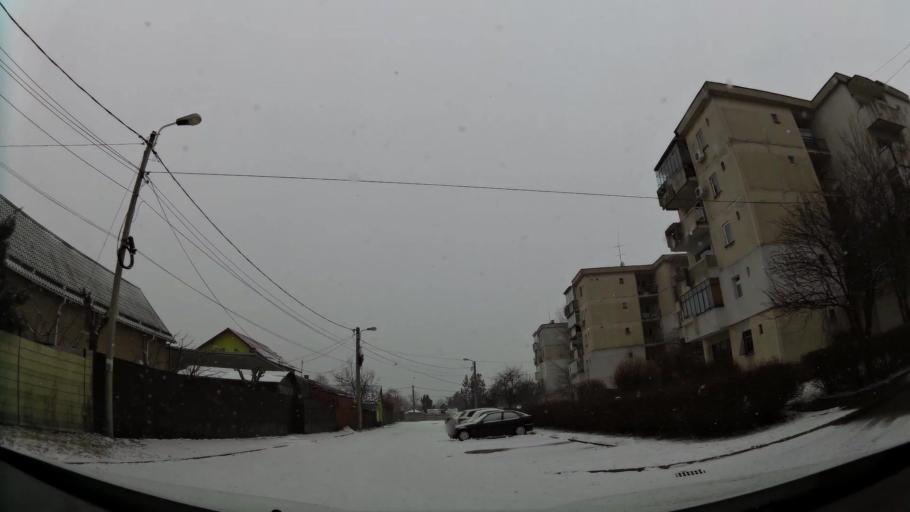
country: RO
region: Prahova
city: Ploiesti
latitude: 44.9285
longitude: 26.0098
